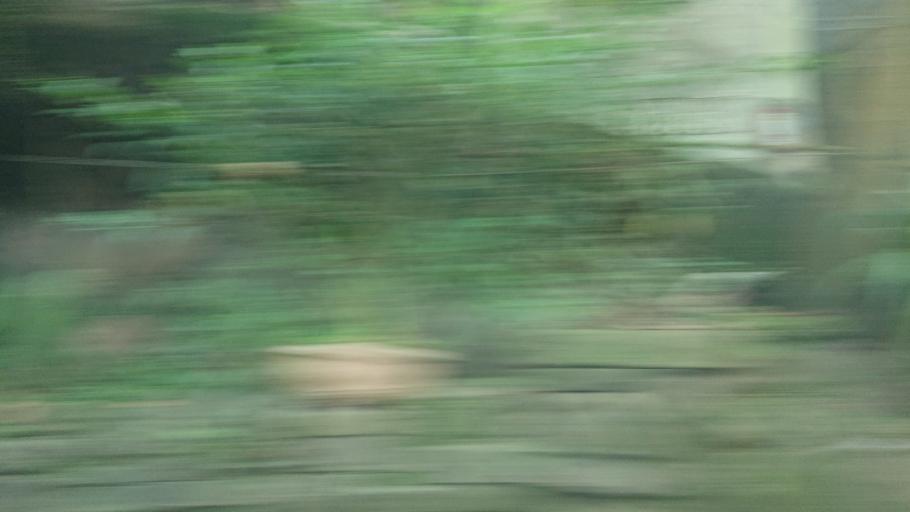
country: TW
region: Taiwan
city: Daxi
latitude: 24.8690
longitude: 121.4144
